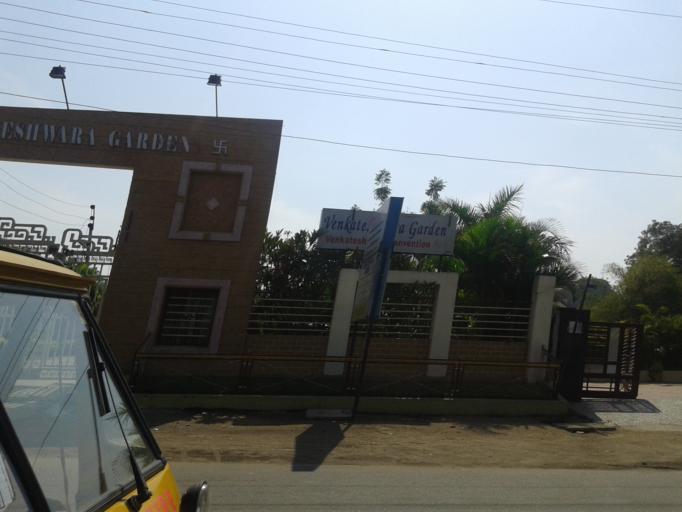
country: IN
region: Telangana
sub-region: Warangal
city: Warangal
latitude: 17.9983
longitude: 79.5865
